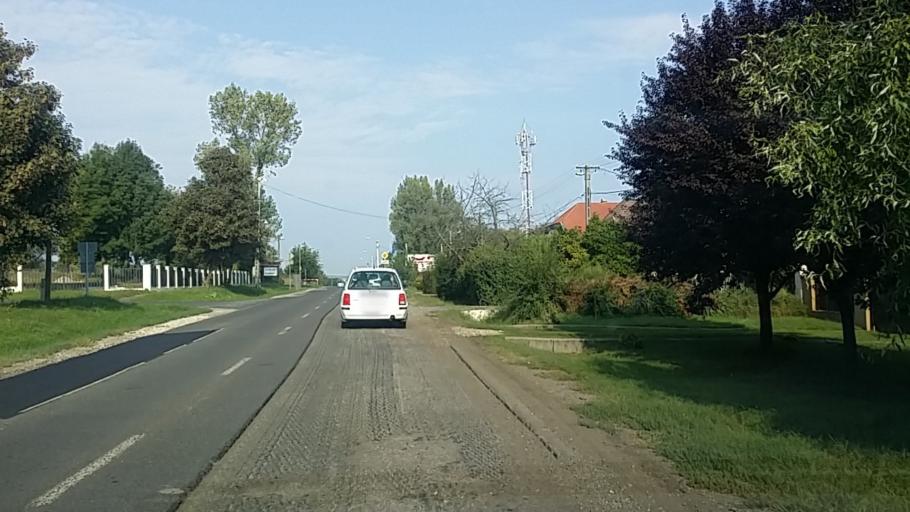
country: HU
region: Pest
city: Aszod
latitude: 47.6407
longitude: 19.4680
